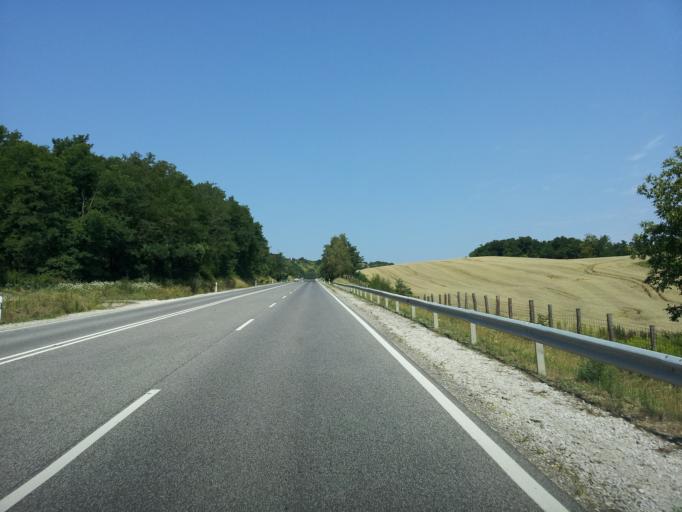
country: HU
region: Zala
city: Pacsa
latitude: 46.8188
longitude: 16.9804
